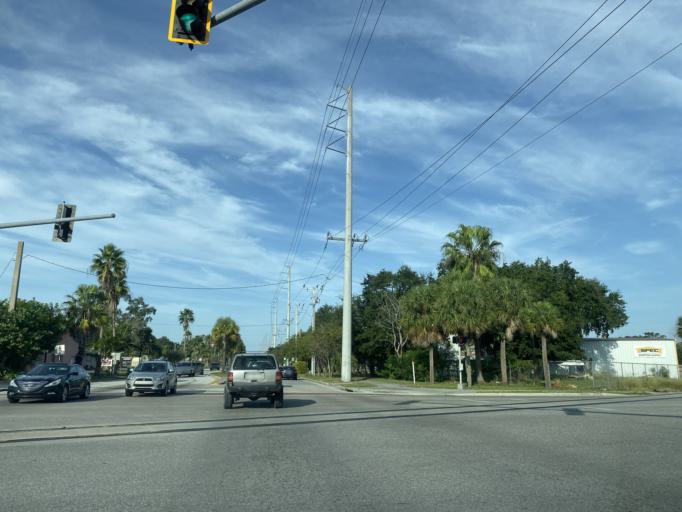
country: US
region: Florida
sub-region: Manatee County
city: Bradenton
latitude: 27.4917
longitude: -82.5547
